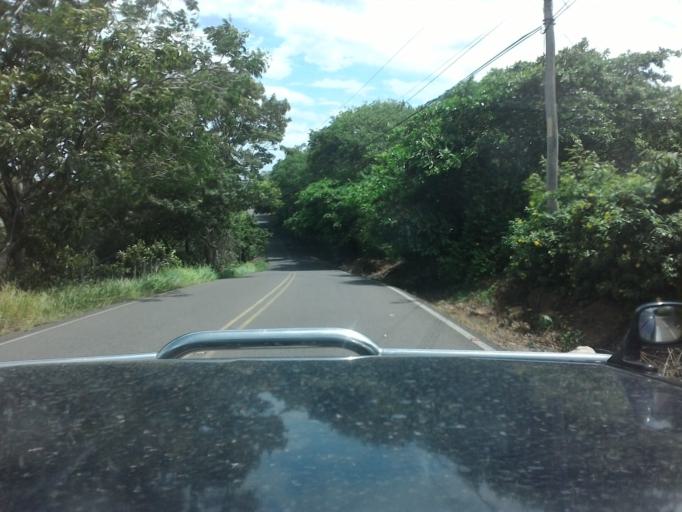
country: CR
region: Puntarenas
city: Miramar
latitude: 10.1181
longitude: -84.8267
